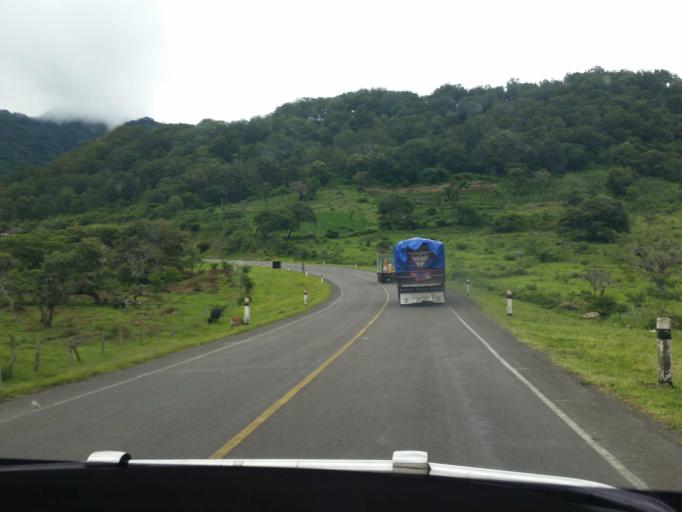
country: NI
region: Jinotega
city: Jinotega
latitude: 13.0621
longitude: -85.9952
